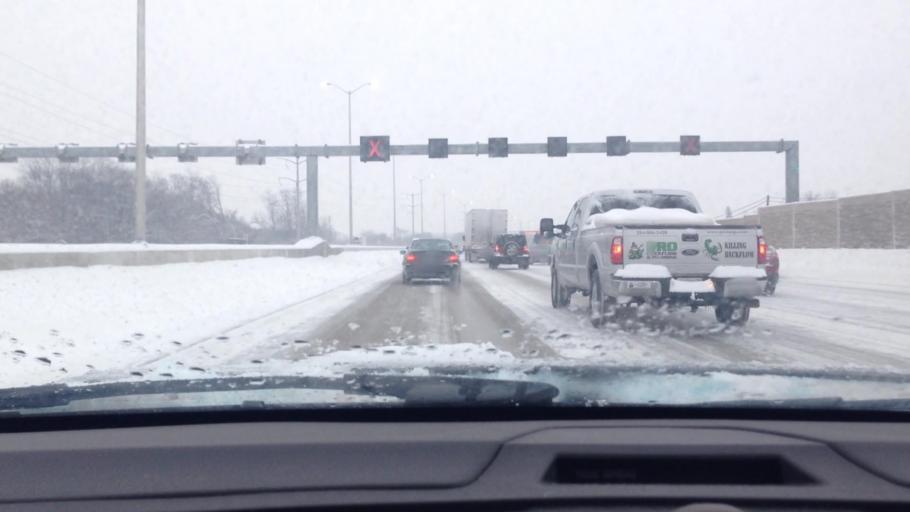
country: US
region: Illinois
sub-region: Cook County
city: South Barrington
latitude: 42.0644
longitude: -88.1075
